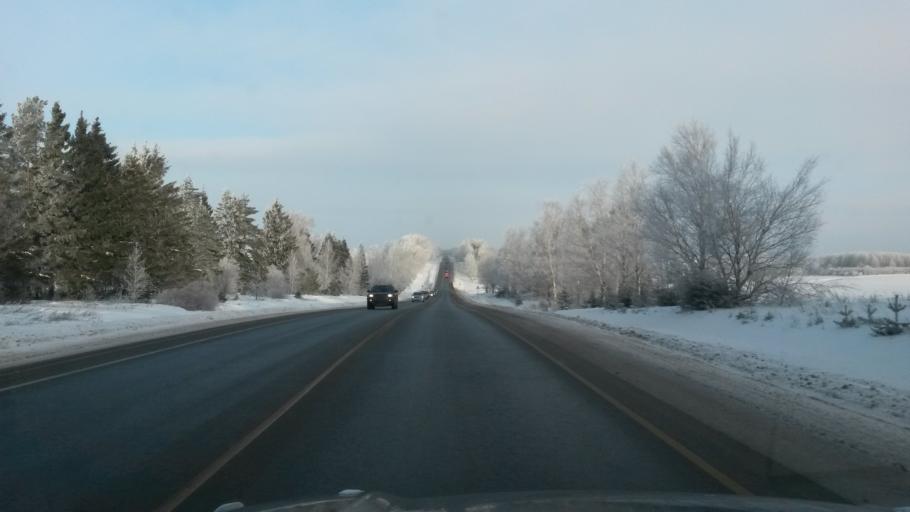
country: RU
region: Vladimir
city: Bogolyubovo
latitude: 56.2393
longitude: 40.4519
